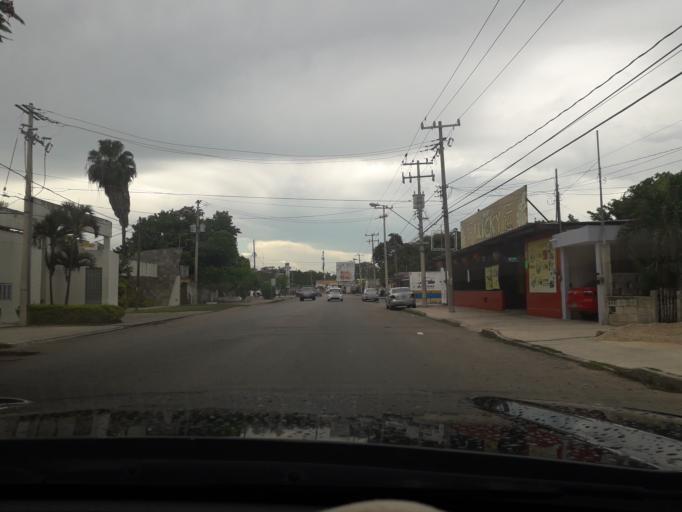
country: MX
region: Yucatan
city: Merida
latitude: 20.9534
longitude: -89.6493
